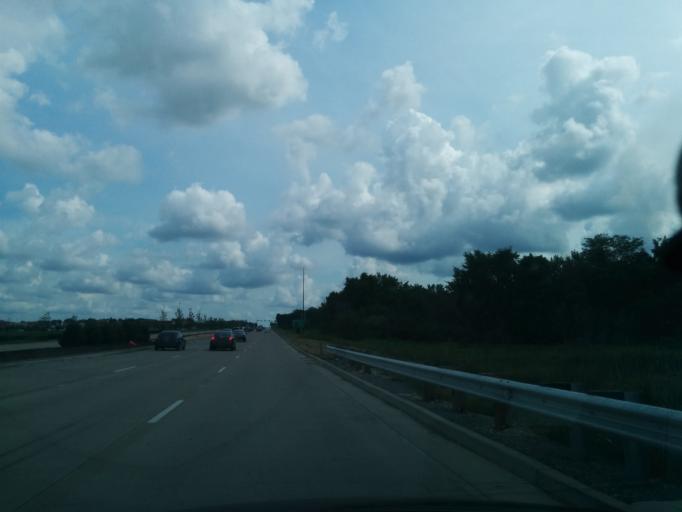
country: US
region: Illinois
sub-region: Cook County
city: Orland Hills
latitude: 41.5841
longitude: -87.8523
